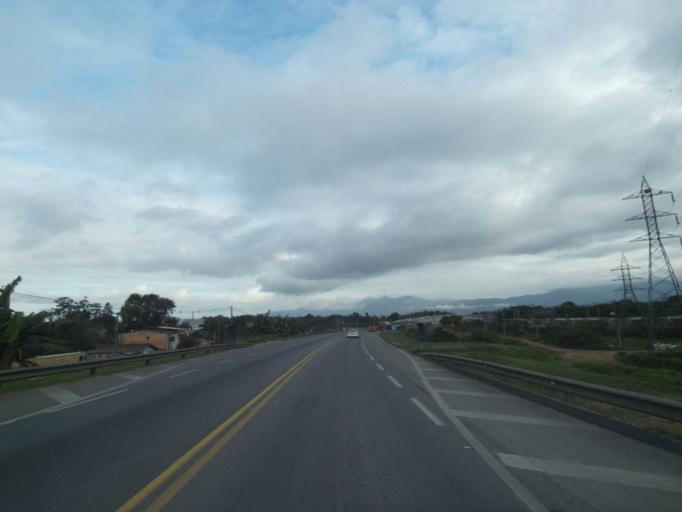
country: BR
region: Parana
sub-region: Paranagua
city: Paranagua
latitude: -25.5531
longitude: -48.5621
